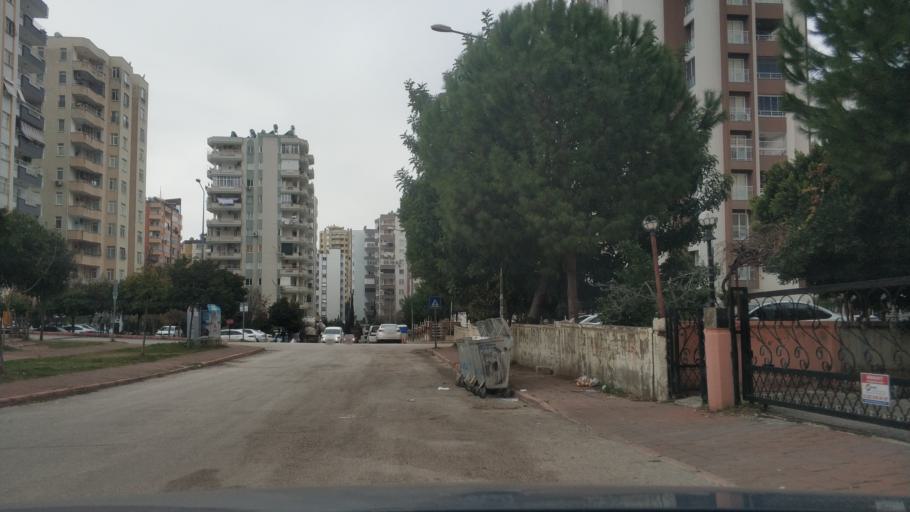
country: TR
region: Adana
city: Seyhan
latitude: 37.0552
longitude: 35.2799
